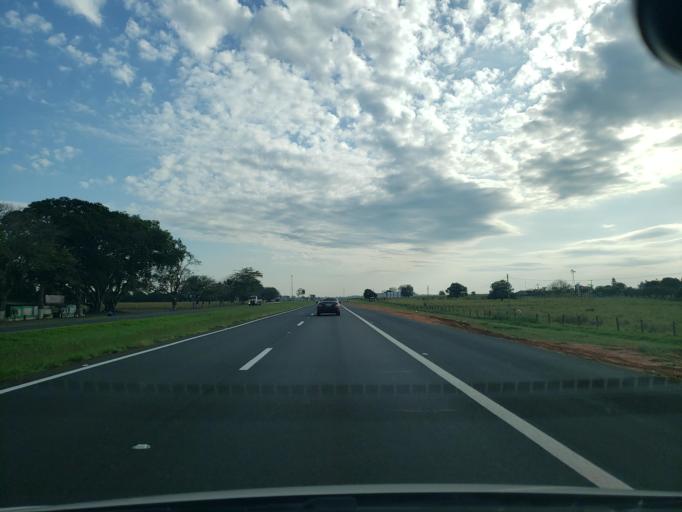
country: BR
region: Sao Paulo
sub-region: Guararapes
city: Guararapes
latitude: -21.2048
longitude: -50.6224
